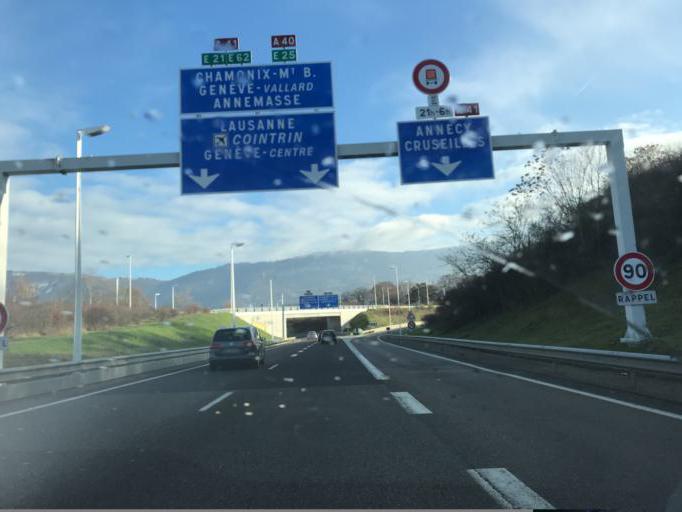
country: FR
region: Rhone-Alpes
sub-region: Departement de la Haute-Savoie
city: Neydens
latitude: 46.1321
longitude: 6.0967
